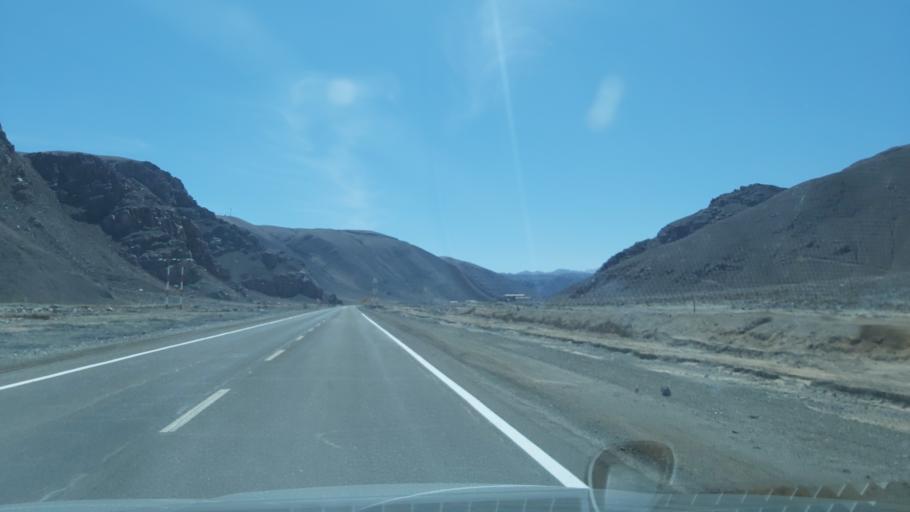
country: CL
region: Atacama
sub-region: Provincia de Chanaral
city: Diego de Almagro
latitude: -26.3387
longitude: -69.8349
